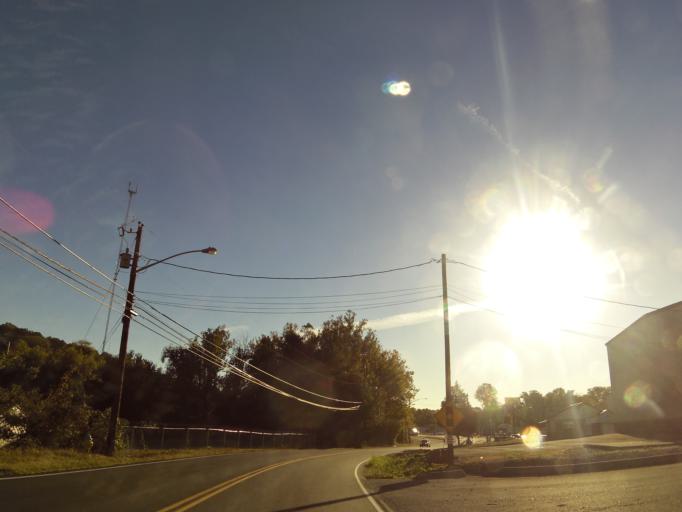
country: US
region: Tennessee
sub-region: Knox County
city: Knoxville
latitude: 36.0057
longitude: -83.9525
